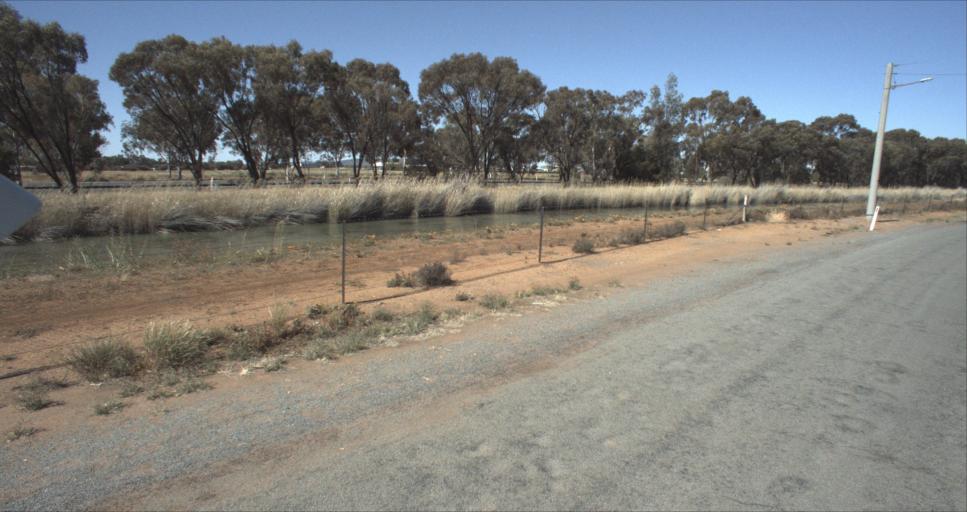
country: AU
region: New South Wales
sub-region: Leeton
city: Leeton
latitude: -34.5483
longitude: 146.3791
